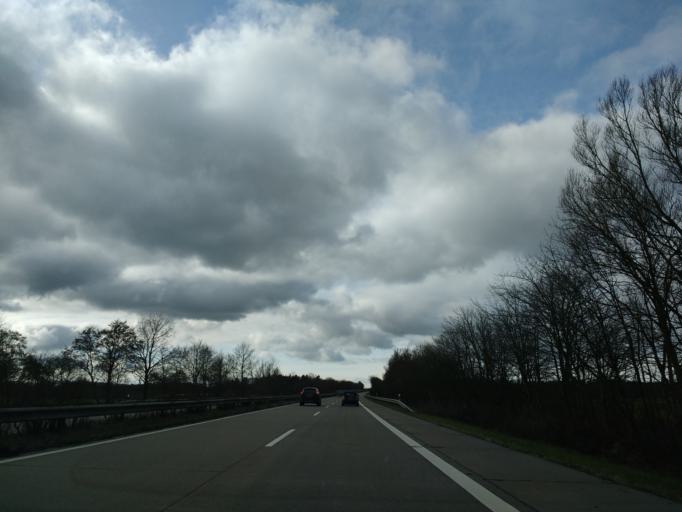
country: DE
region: Lower Saxony
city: Midlum
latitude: 53.7625
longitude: 8.6915
